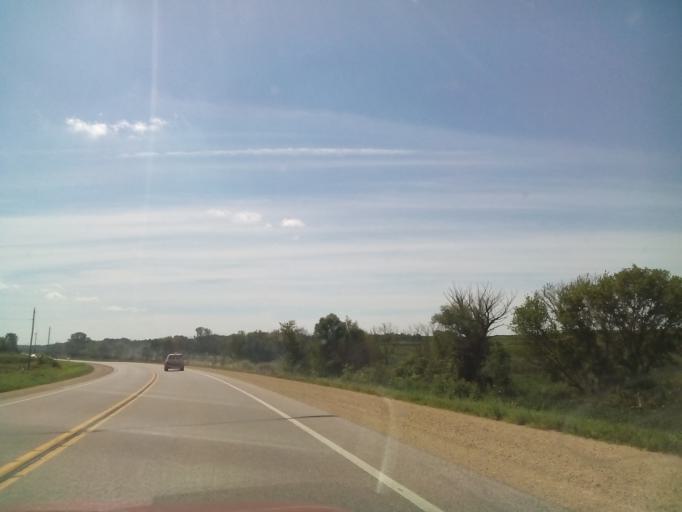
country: US
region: Wisconsin
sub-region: Green County
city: Monticello
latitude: 42.7717
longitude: -89.6276
